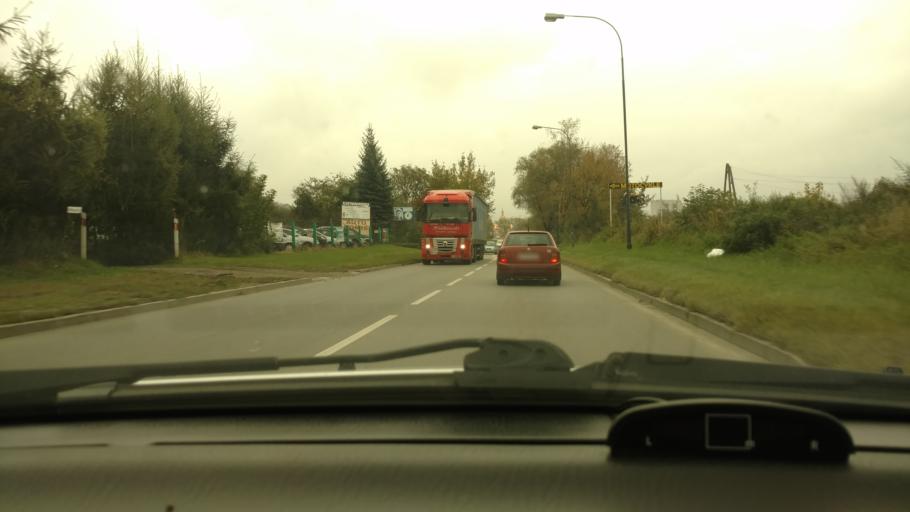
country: PL
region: Lesser Poland Voivodeship
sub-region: Powiat nowosadecki
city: Nowy Sacz
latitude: 49.6356
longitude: 20.7054
